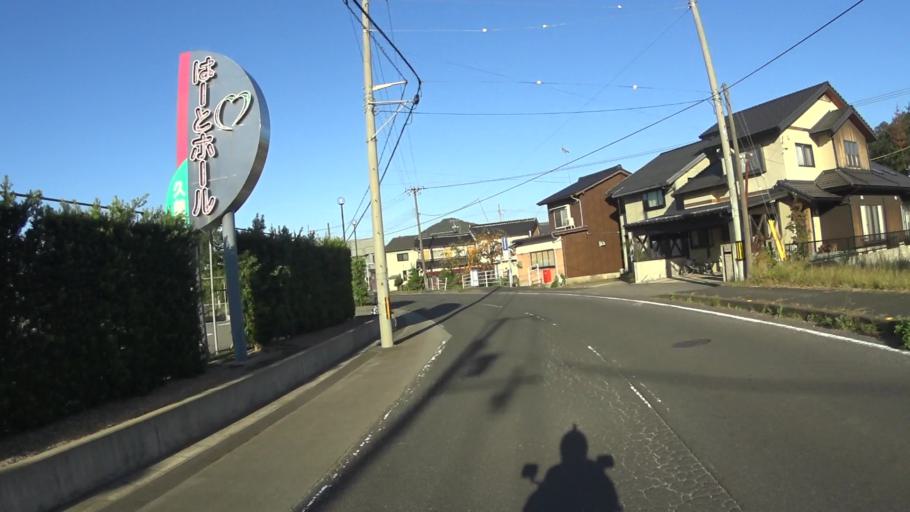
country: JP
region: Hyogo
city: Toyooka
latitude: 35.6025
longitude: 134.8935
